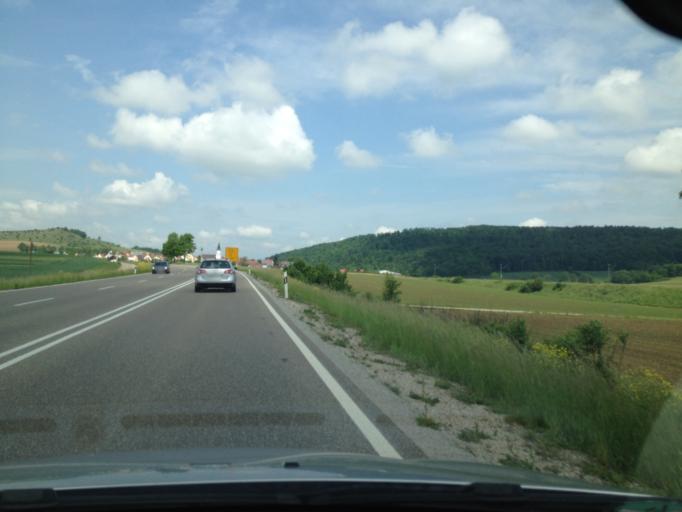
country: DE
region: Bavaria
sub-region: Swabia
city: Harburg
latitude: 48.7946
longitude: 10.6623
